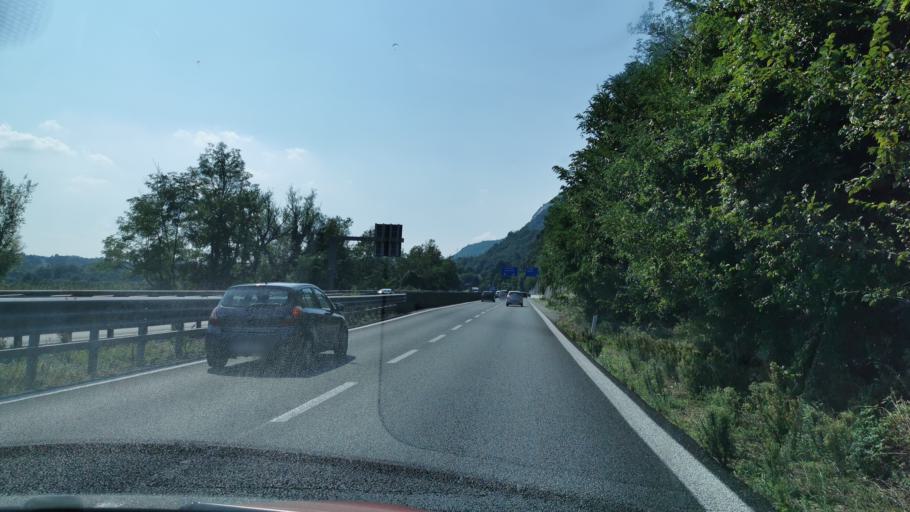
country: IT
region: Lombardy
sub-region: Provincia di Lecco
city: Civate
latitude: 45.8245
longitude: 9.3315
